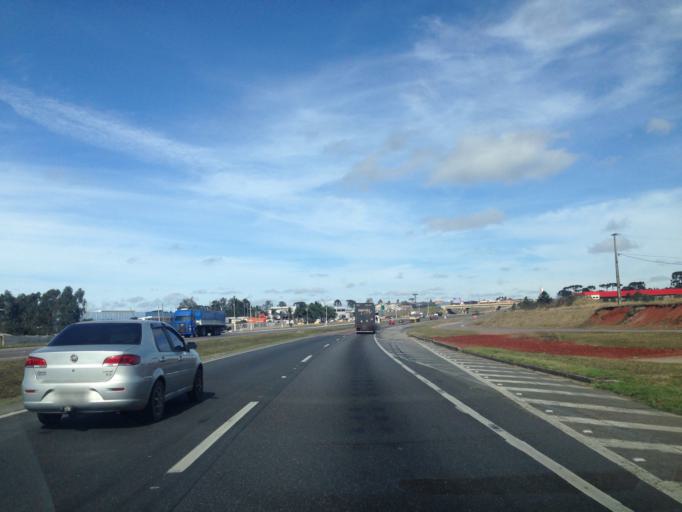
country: BR
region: Parana
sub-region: Sao Jose Dos Pinhais
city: Sao Jose dos Pinhais
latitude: -25.5552
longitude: -49.1499
